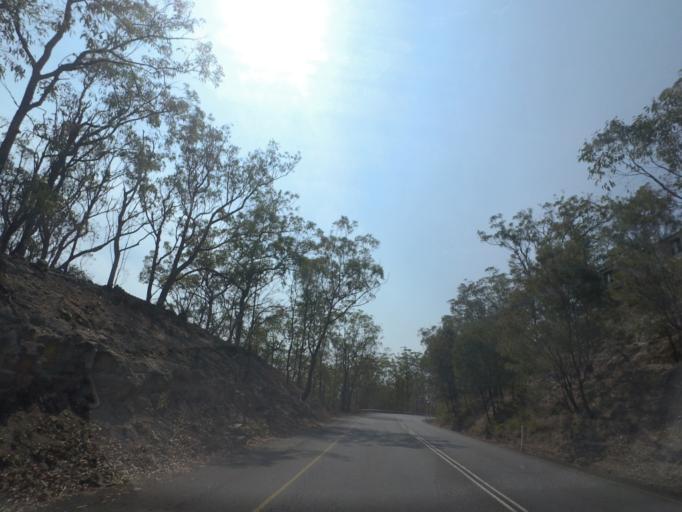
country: AU
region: Queensland
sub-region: Brisbane
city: Nathan
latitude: -27.5557
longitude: 153.0519
